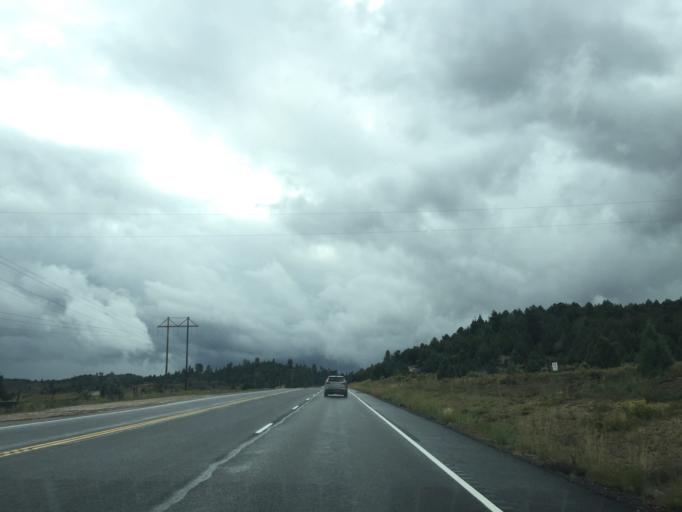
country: US
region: Utah
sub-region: Garfield County
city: Panguitch
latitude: 37.5043
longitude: -112.5000
